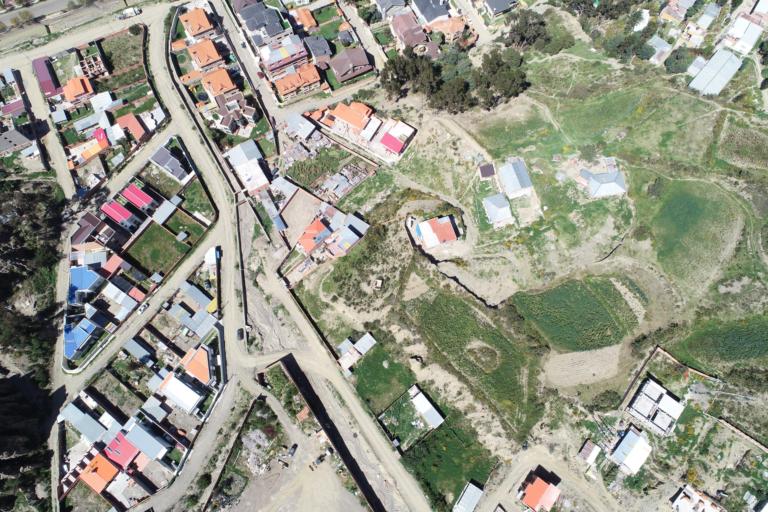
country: BO
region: La Paz
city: La Paz
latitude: -16.5087
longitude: -68.0581
